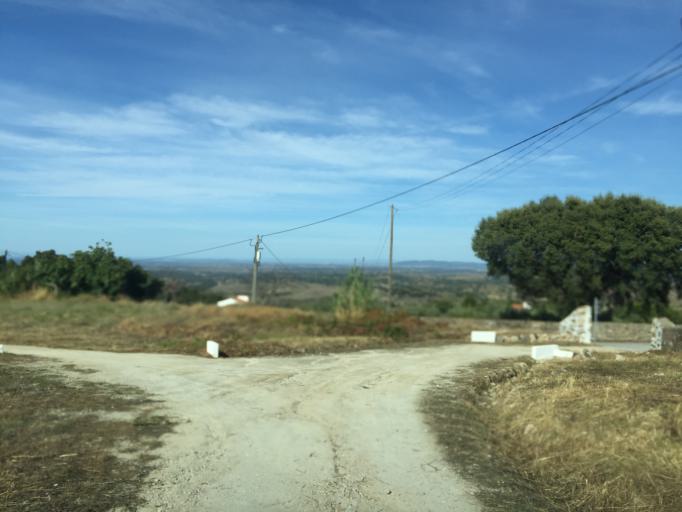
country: PT
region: Portalegre
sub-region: Marvao
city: Marvao
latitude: 39.4028
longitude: -7.3752
